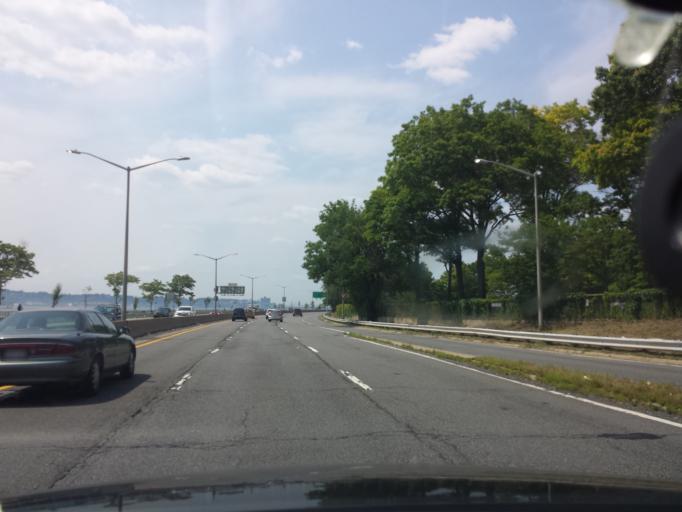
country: US
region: New York
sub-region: Kings County
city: Bensonhurst
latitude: 40.6123
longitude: -74.0374
